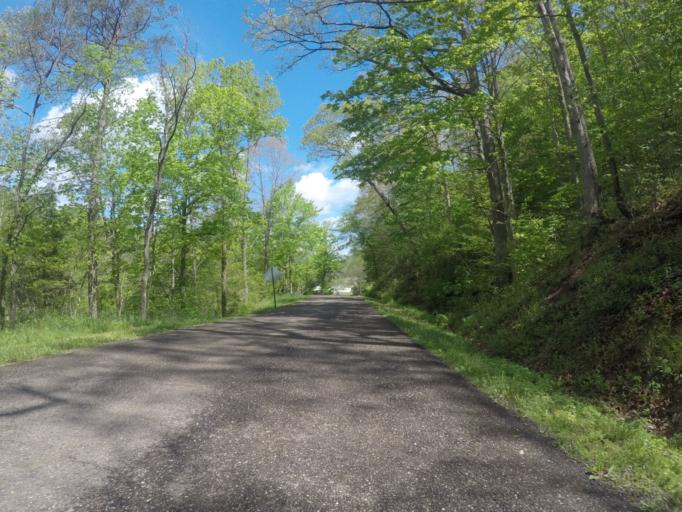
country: US
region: West Virginia
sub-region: Cabell County
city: Huntington
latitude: 38.5157
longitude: -82.4391
